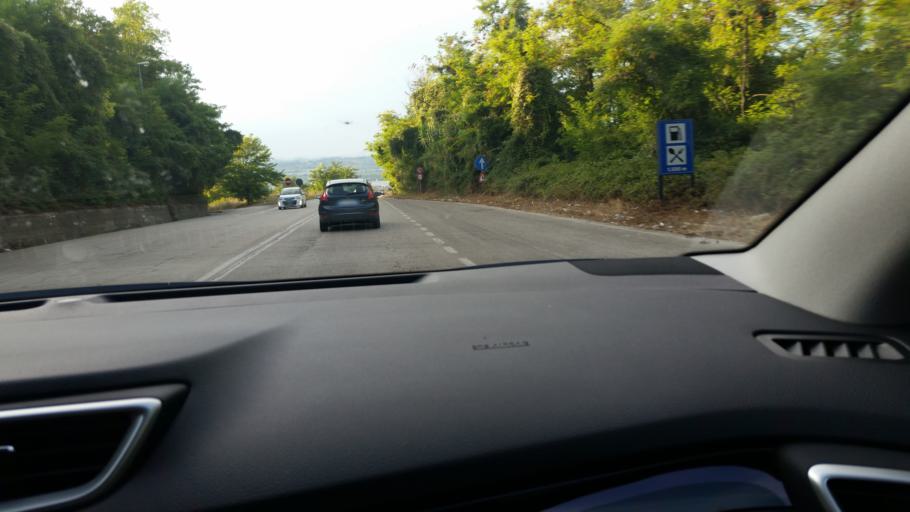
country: IT
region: Abruzzo
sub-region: Provincia di Chieti
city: Chieti
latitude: 42.3623
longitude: 14.1593
